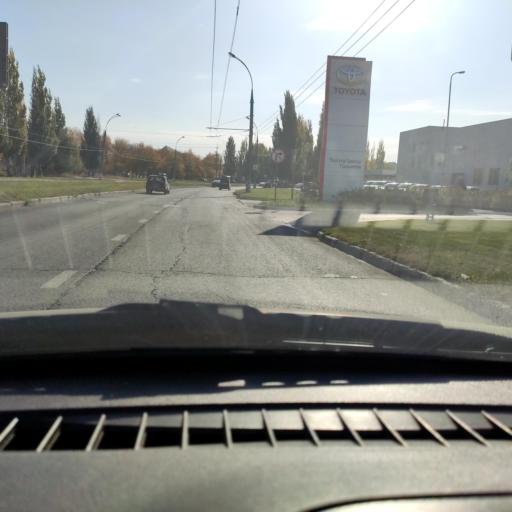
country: RU
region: Samara
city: Tol'yatti
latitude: 53.5447
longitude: 49.2775
